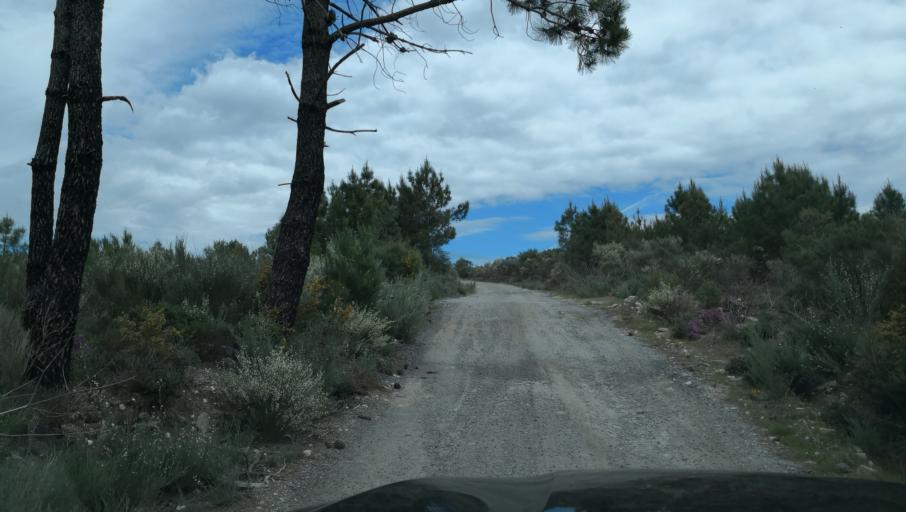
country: PT
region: Vila Real
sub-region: Vila Real
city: Vila Real
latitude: 41.3644
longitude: -7.7005
